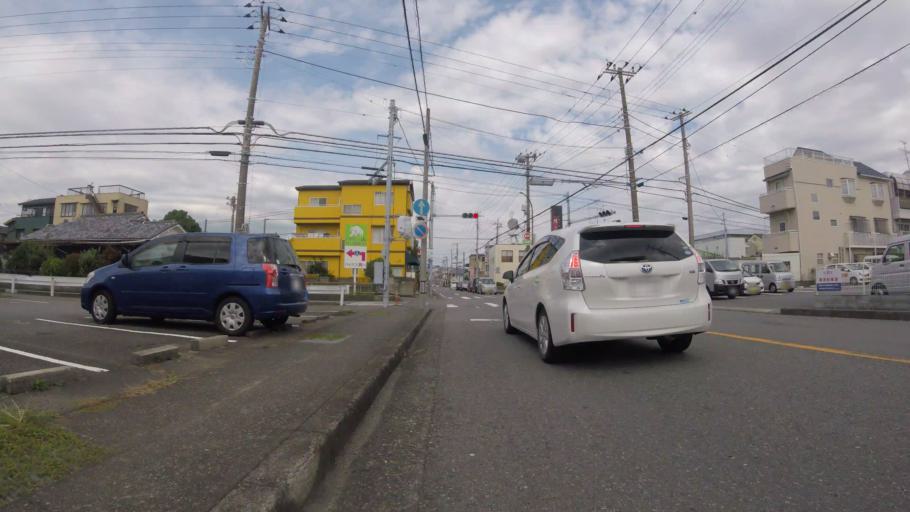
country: JP
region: Shizuoka
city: Numazu
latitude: 35.1183
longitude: 138.8626
